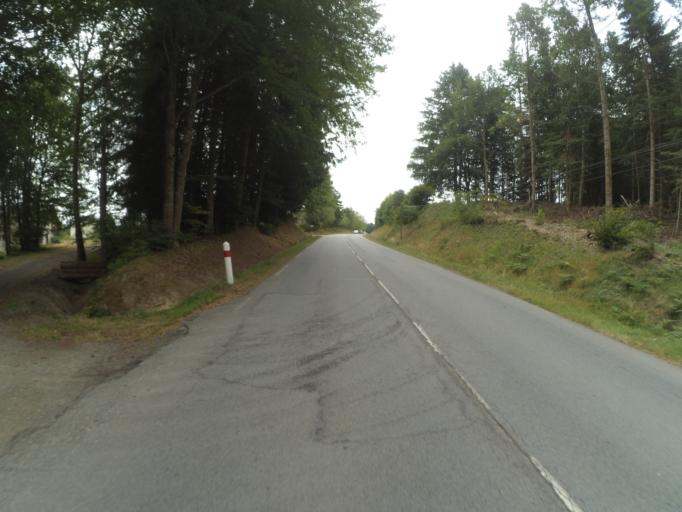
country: FR
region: Limousin
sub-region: Departement de la Correze
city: Ussel
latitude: 45.5776
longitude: 2.2940
